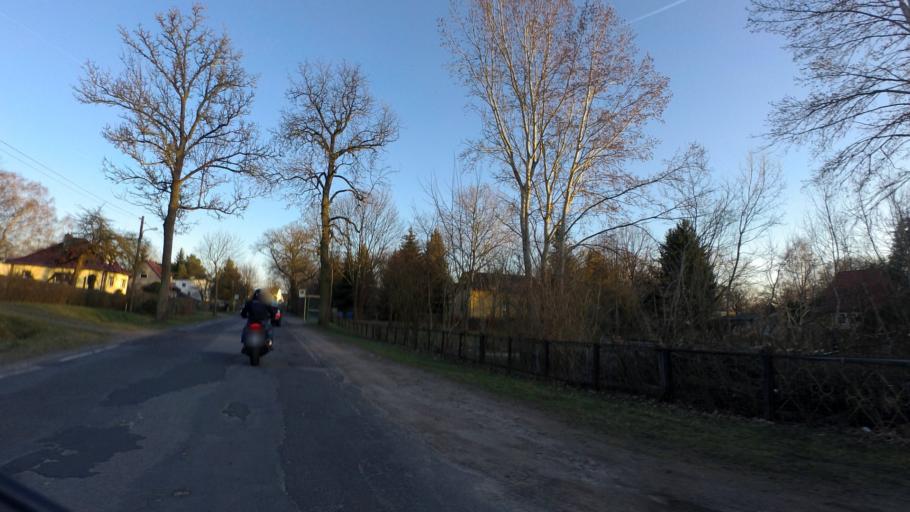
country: DE
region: Berlin
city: Hellersdorf
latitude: 52.5585
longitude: 13.6316
